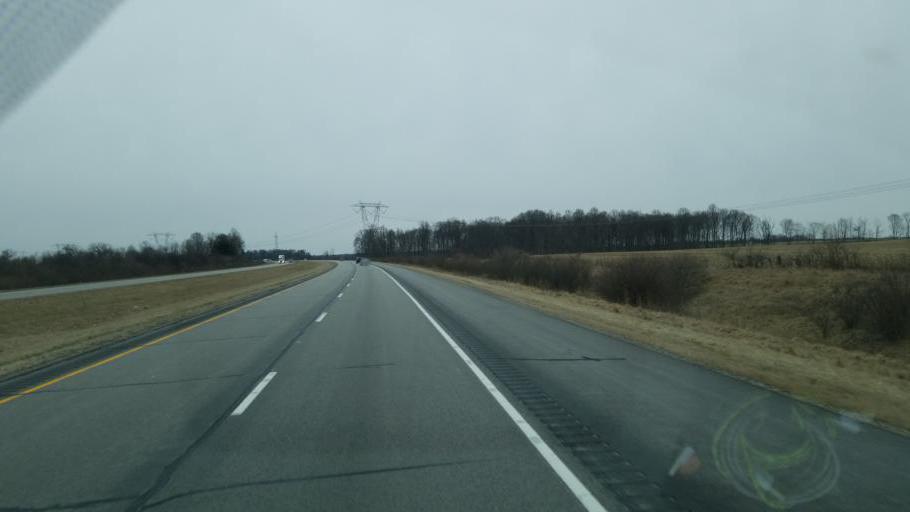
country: US
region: Indiana
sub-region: Marshall County
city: Argos
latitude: 41.2132
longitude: -86.2611
